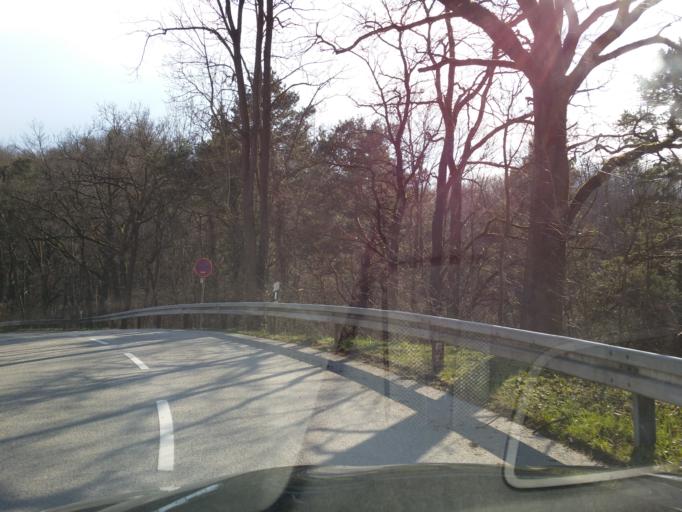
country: DE
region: Bavaria
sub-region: Lower Bavaria
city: Landshut
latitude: 48.5249
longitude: 12.1315
